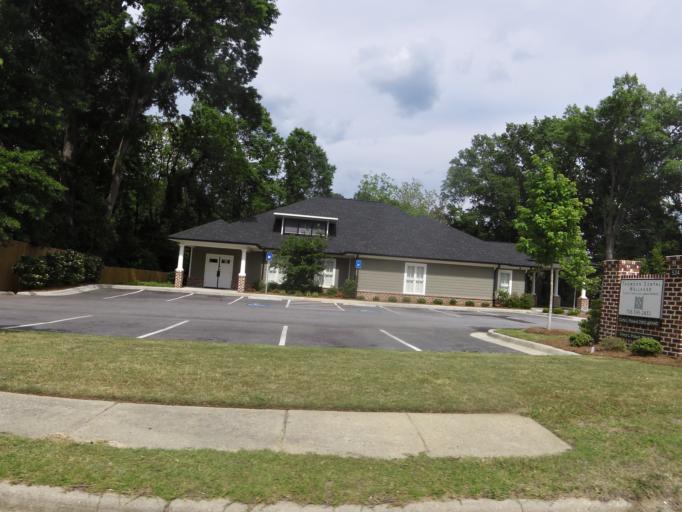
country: US
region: Georgia
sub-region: McDuffie County
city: Thomson
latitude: 33.4578
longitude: -82.4985
